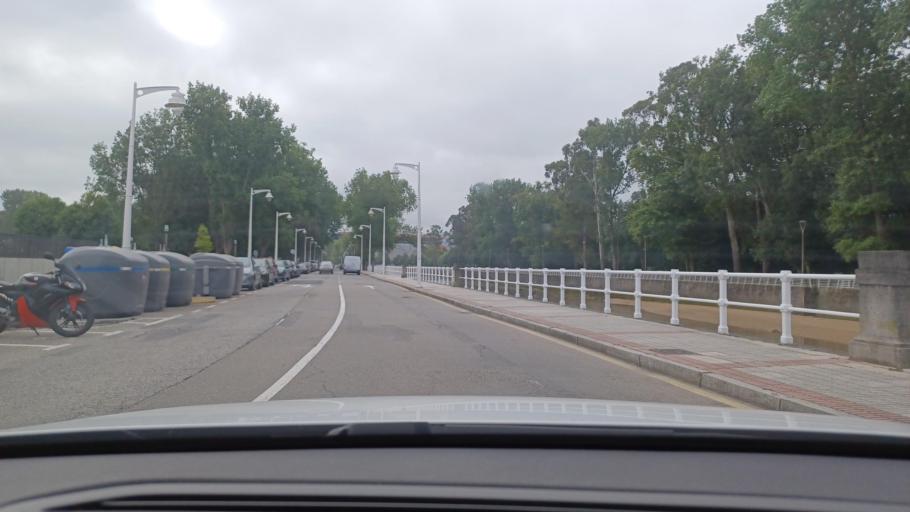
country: ES
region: Asturias
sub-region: Province of Asturias
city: Gijon
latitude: 43.5403
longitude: -5.6430
